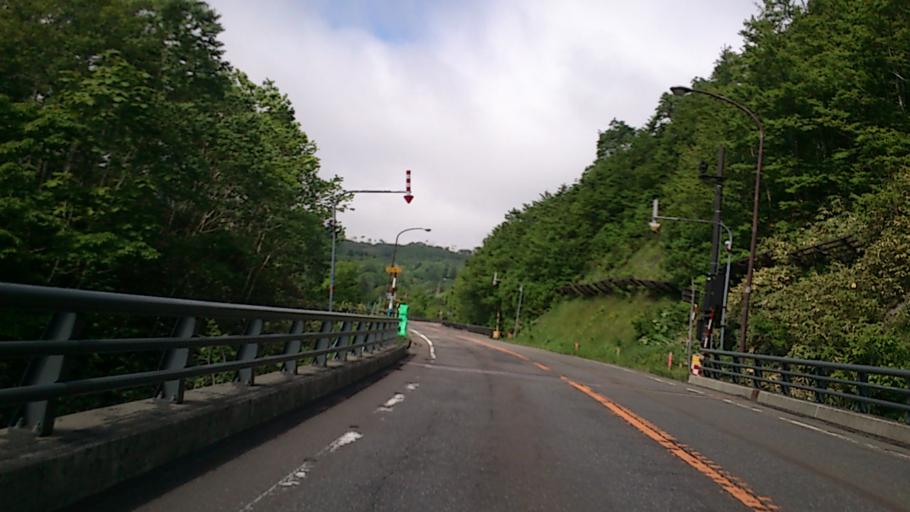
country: JP
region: Hokkaido
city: Shiraoi
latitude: 42.7125
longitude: 141.2043
